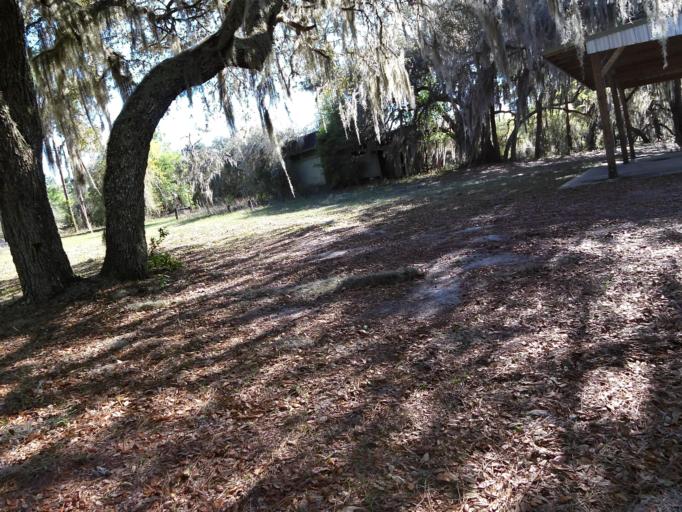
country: US
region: Florida
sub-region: Clay County
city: Keystone Heights
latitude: 29.8197
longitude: -82.0149
